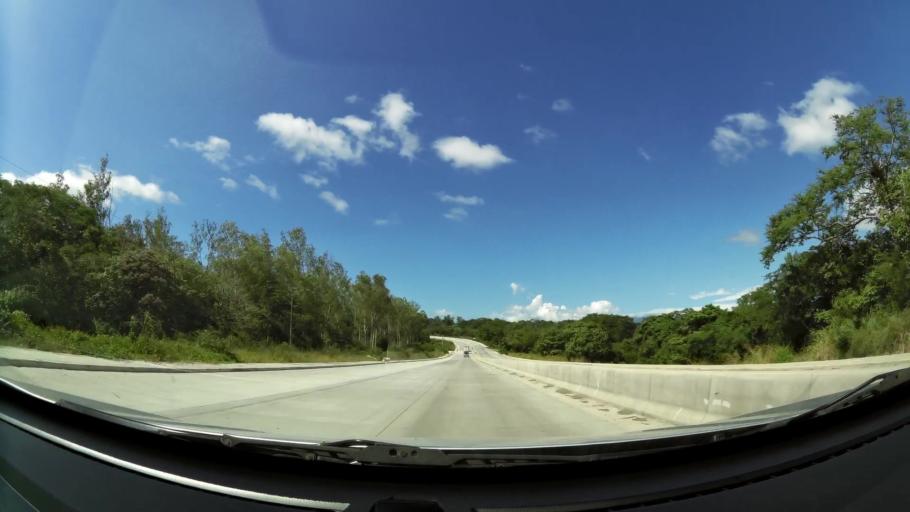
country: CR
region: Guanacaste
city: Bagaces
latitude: 10.5325
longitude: -85.2871
